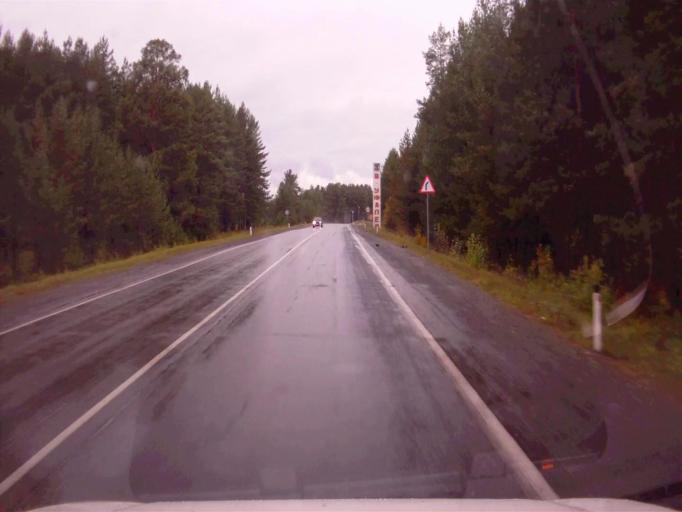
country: RU
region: Chelyabinsk
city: Verkhniy Ufaley
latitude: 56.0269
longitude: 60.2908
